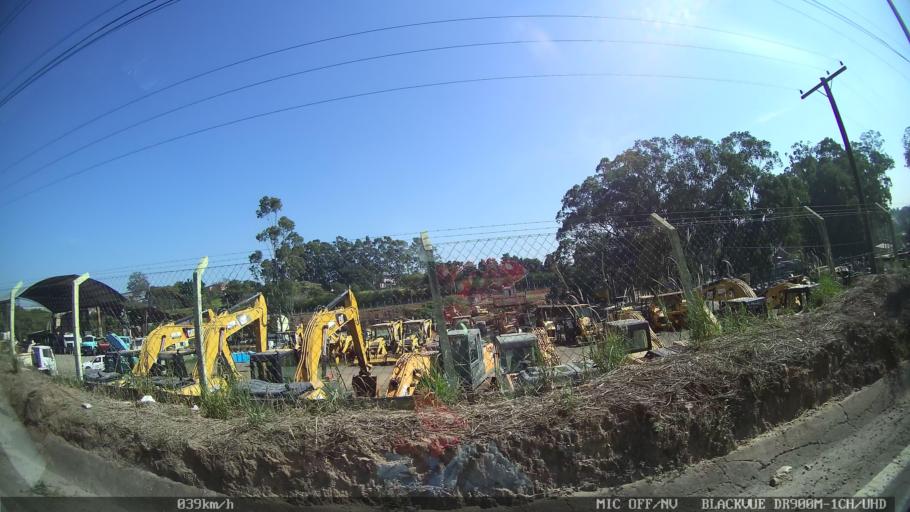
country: BR
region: Sao Paulo
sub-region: Valinhos
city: Valinhos
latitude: -23.0030
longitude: -47.0889
